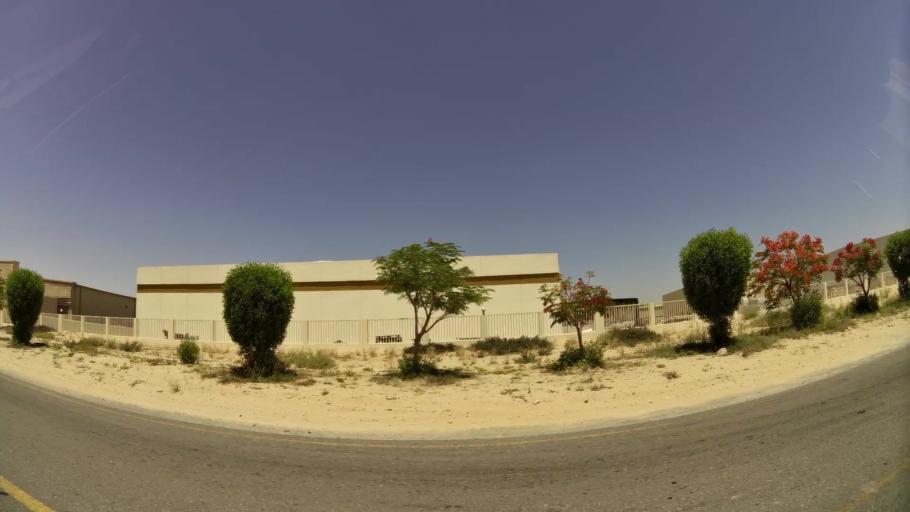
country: AE
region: Dubai
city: Dubai
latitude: 24.9778
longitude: 55.1883
